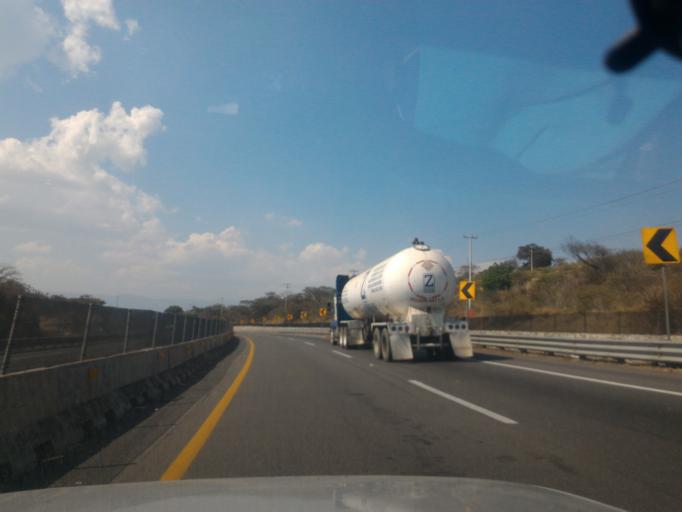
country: MX
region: Jalisco
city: San Andres Ixtlan
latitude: 19.8408
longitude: -103.5012
